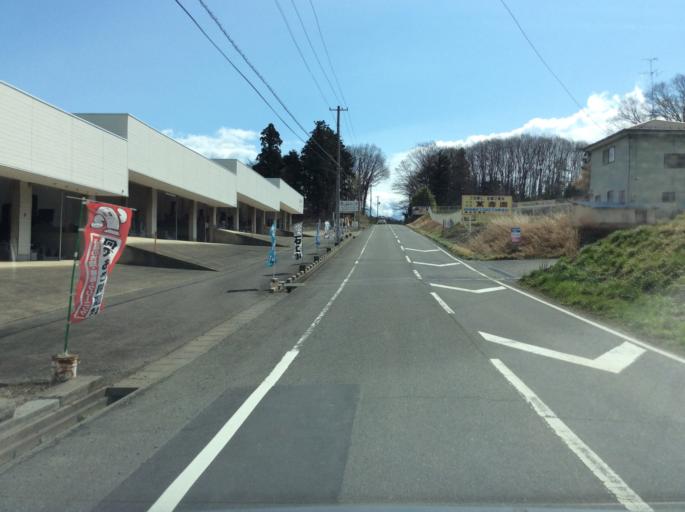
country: JP
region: Fukushima
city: Koriyama
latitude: 37.3523
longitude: 140.4192
